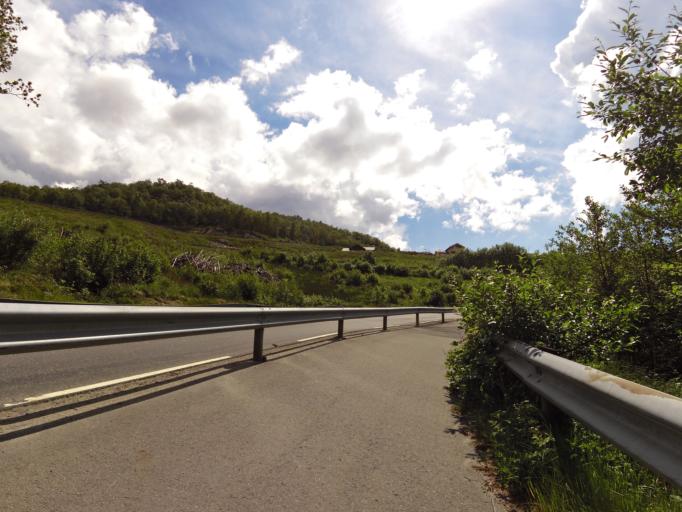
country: NO
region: Vest-Agder
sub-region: Lyngdal
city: Lyngdal
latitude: 58.1159
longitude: 7.0637
